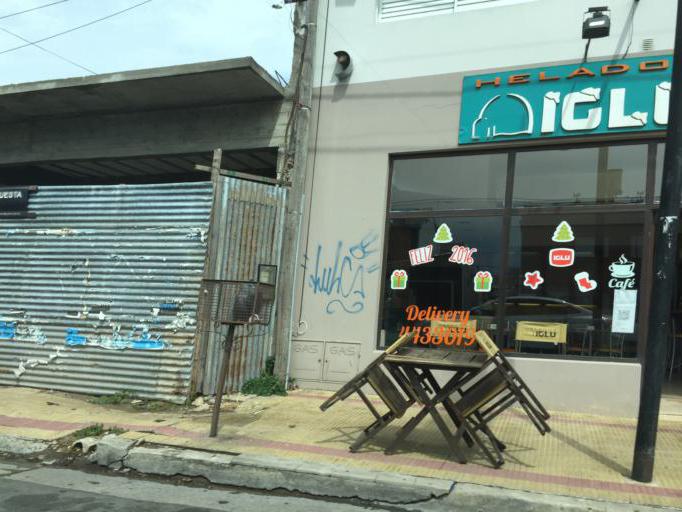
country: AR
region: Buenos Aires
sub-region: Partido de Tandil
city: Tandil
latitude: -37.3250
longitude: -59.1121
